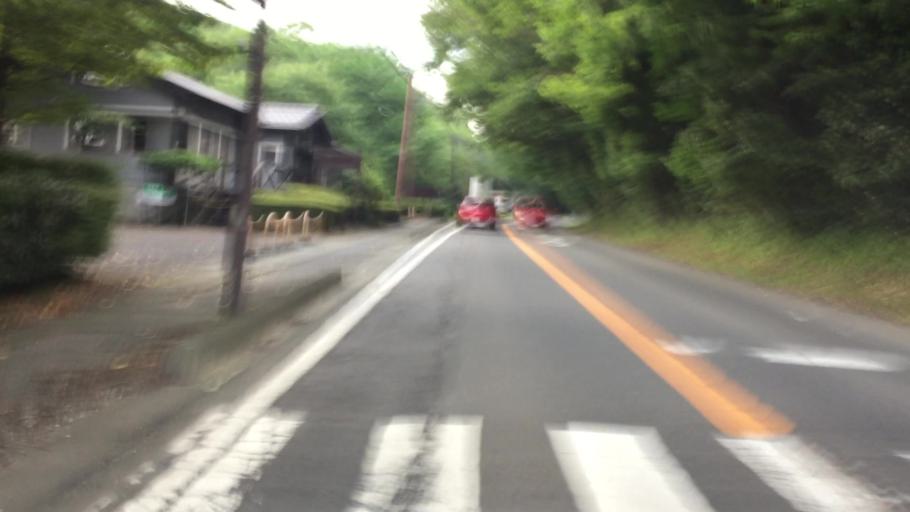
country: JP
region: Tochigi
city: Kuroiso
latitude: 37.0114
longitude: 140.0310
